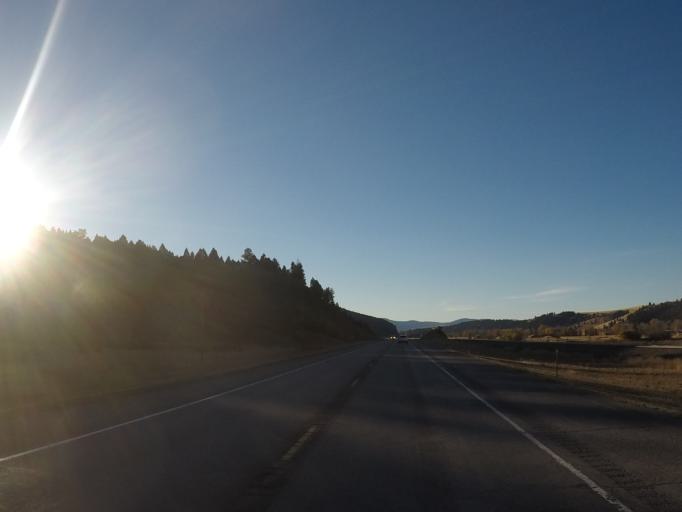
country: US
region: Montana
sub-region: Lewis and Clark County
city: Helena West Side
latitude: 46.5633
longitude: -112.4394
